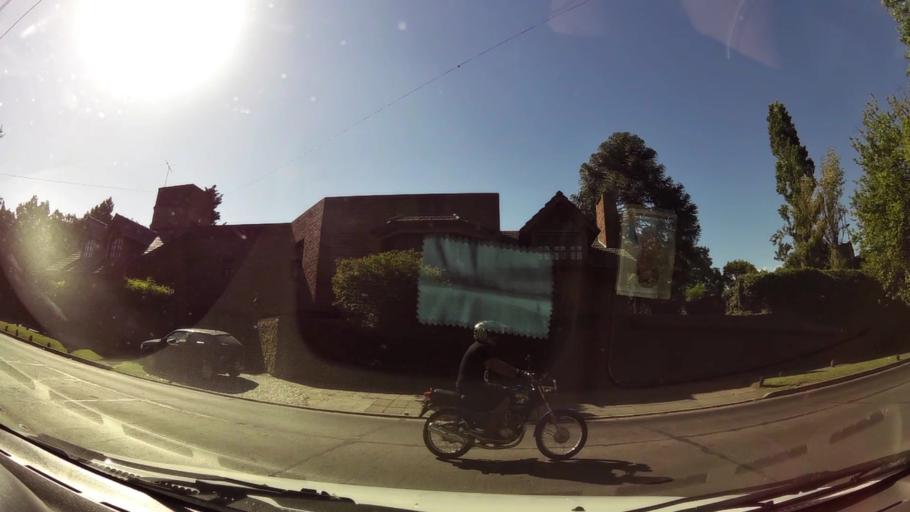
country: AR
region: Buenos Aires
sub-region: Partido de San Isidro
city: San Isidro
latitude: -34.4797
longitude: -58.5522
